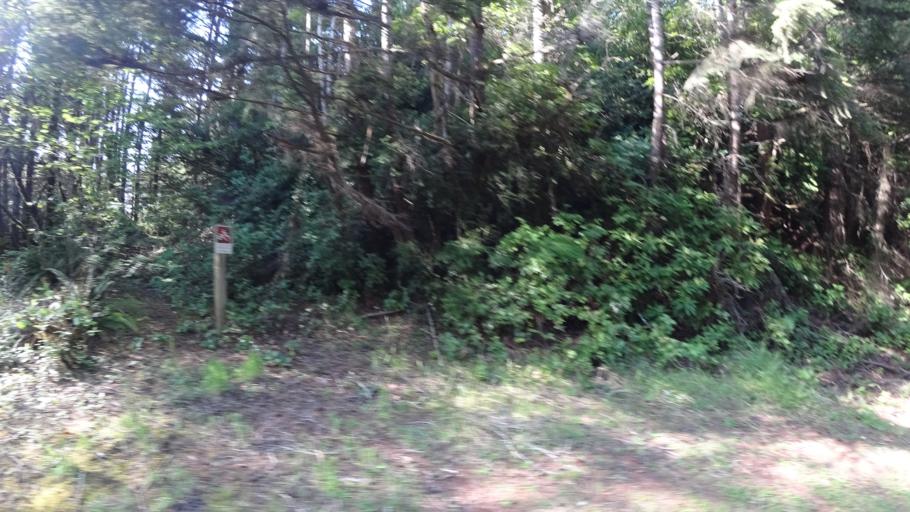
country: US
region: Oregon
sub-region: Douglas County
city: Reedsport
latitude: 43.7463
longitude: -124.1727
